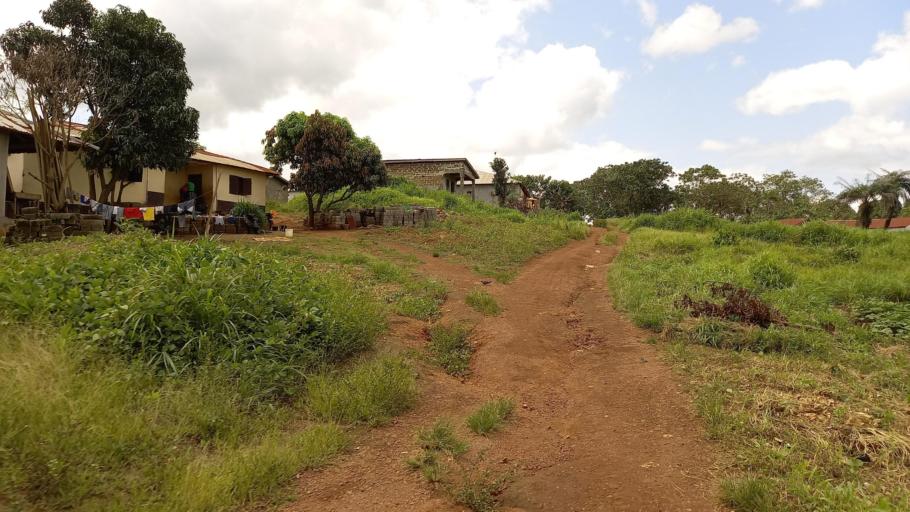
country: SL
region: Northern Province
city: Kamakwie
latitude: 9.5019
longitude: -12.2445
